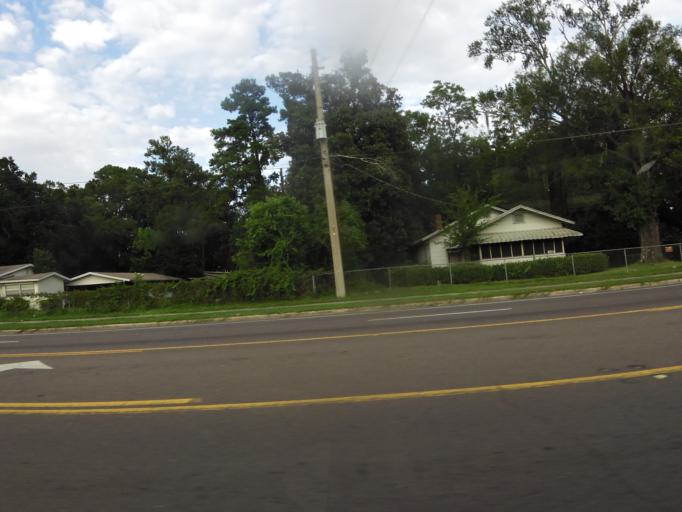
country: US
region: Florida
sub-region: Duval County
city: Jacksonville
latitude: 30.3381
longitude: -81.7521
